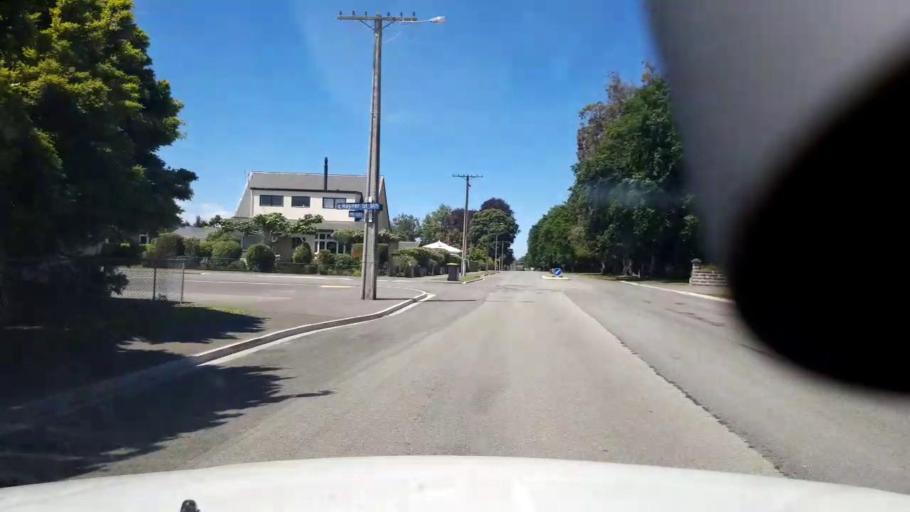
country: NZ
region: Canterbury
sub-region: Timaru District
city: Pleasant Point
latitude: -44.2472
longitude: 171.2850
